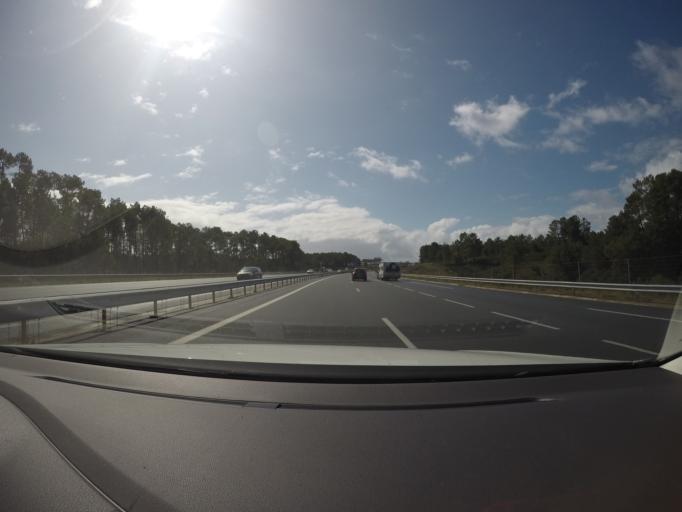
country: FR
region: Aquitaine
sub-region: Departement des Landes
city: Castets
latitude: 43.8779
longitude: -1.1317
